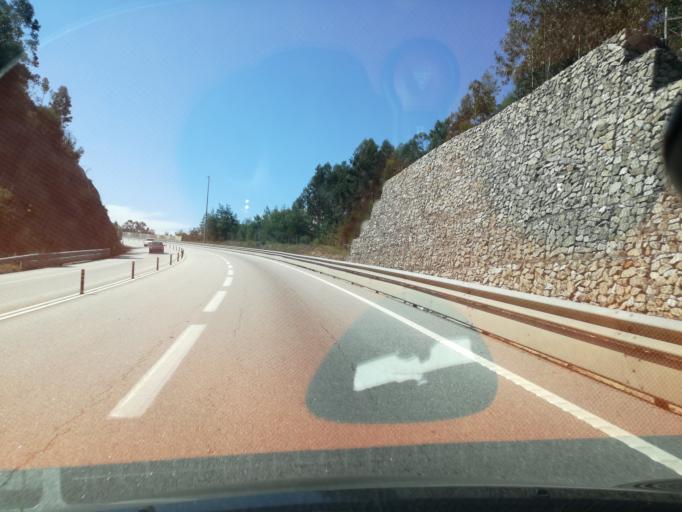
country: PT
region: Viana do Castelo
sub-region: Vila Nova de Cerveira
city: Vila Nova de Cerveira
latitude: 41.9131
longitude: -8.7826
